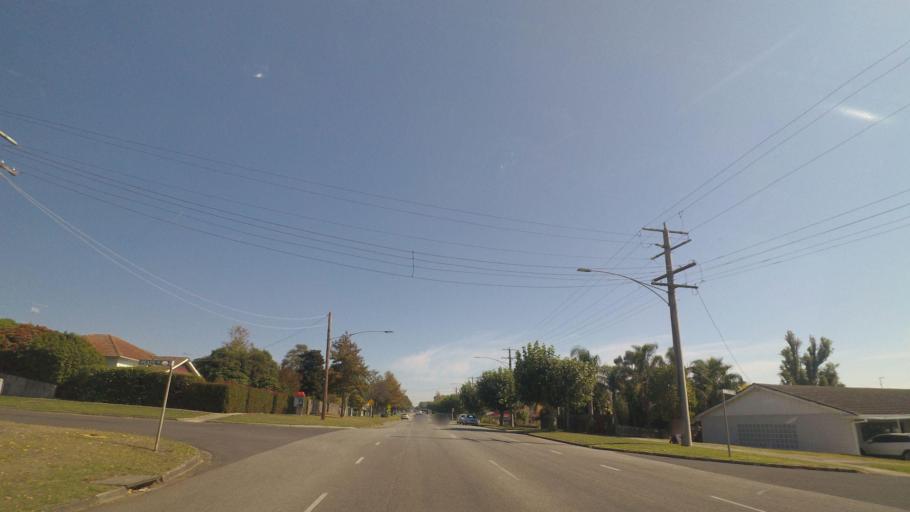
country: AU
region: Victoria
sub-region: Baw Baw
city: Warragul
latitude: -38.1611
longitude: 145.9385
